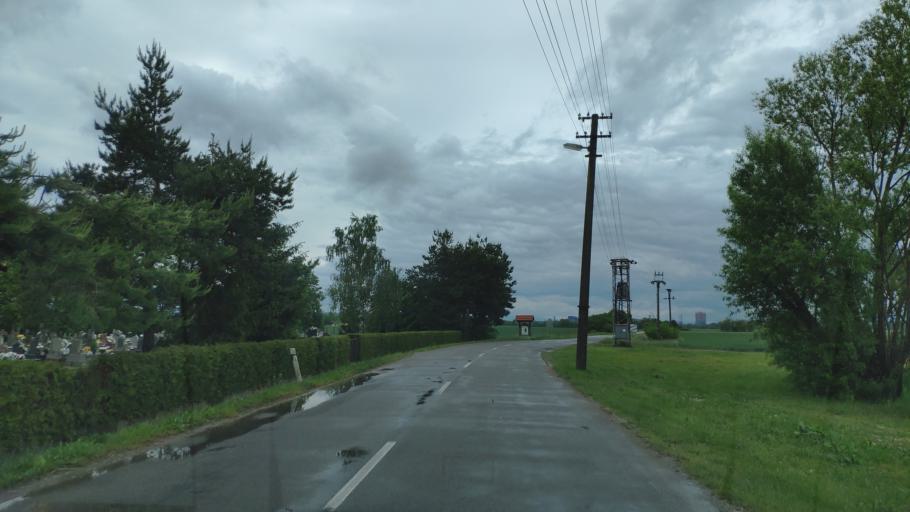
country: SK
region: Kosicky
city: Moldava nad Bodvou
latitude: 48.5765
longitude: 21.1213
